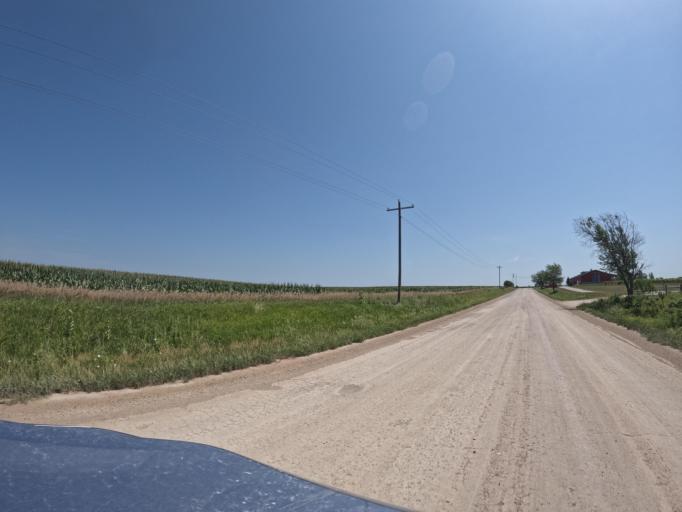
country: US
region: Iowa
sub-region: Henry County
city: Mount Pleasant
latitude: 40.9375
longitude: -91.5190
